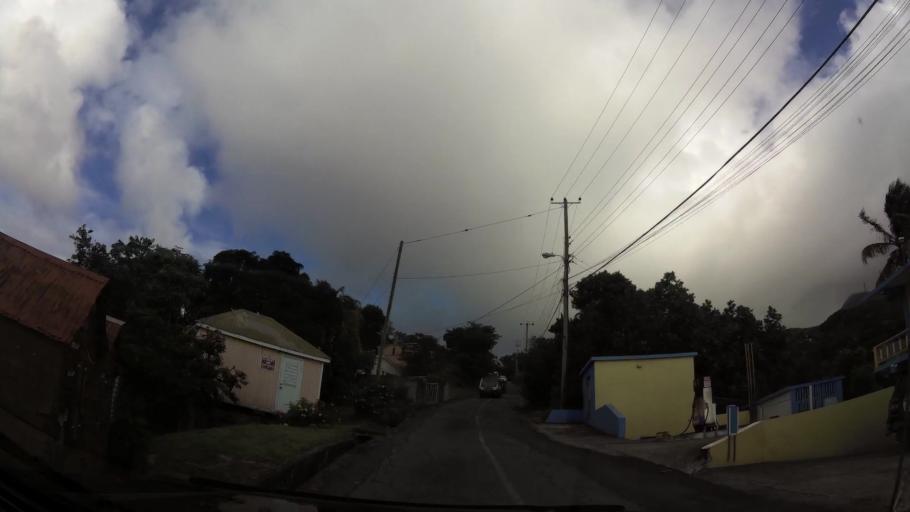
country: MS
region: Saint Peter
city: Saint Peters
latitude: 16.7748
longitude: -62.2142
